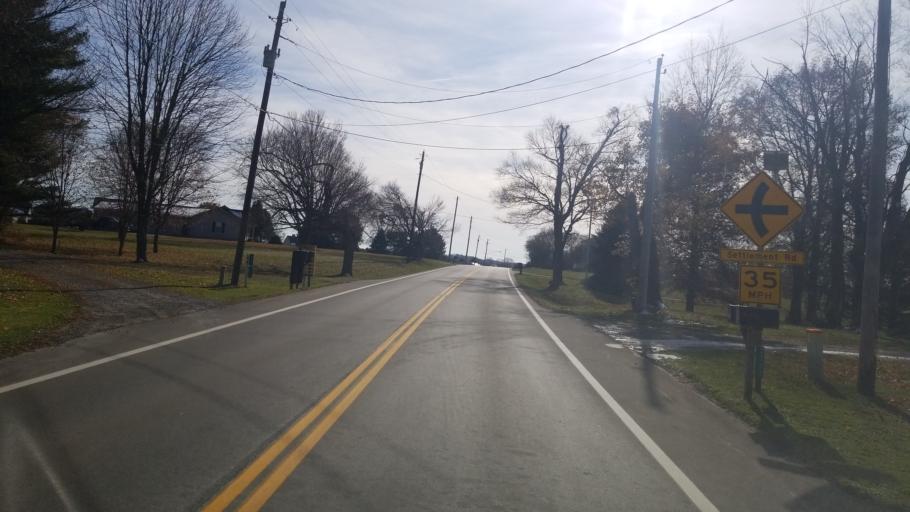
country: US
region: Ohio
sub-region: Huron County
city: Norwalk
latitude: 41.2055
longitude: -82.6351
